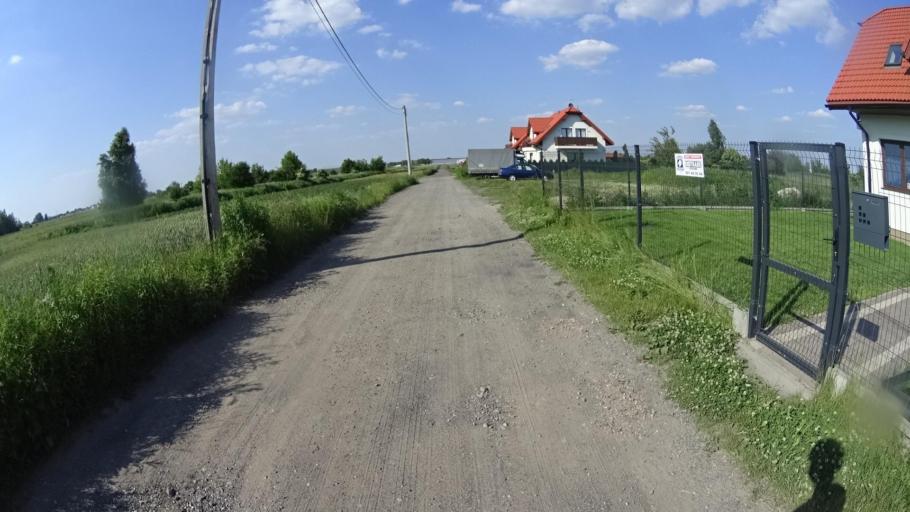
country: PL
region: Masovian Voivodeship
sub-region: Powiat warszawski zachodni
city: Ozarow Mazowiecki
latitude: 52.1940
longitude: 20.7636
